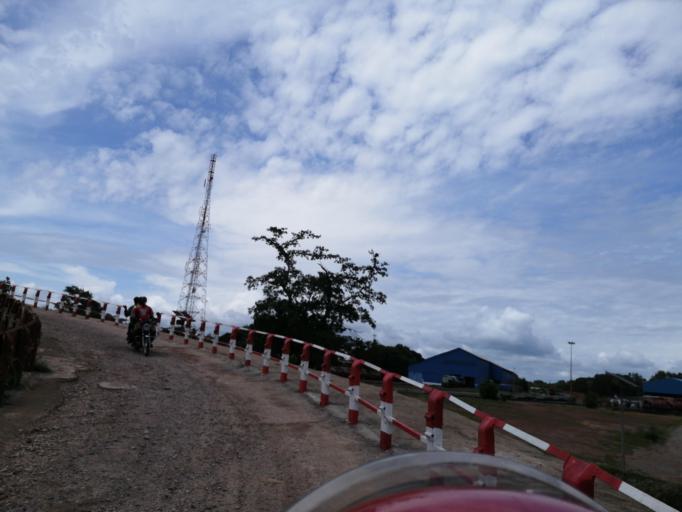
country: SL
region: Northern Province
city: Pepel
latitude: 8.5905
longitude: -13.0569
